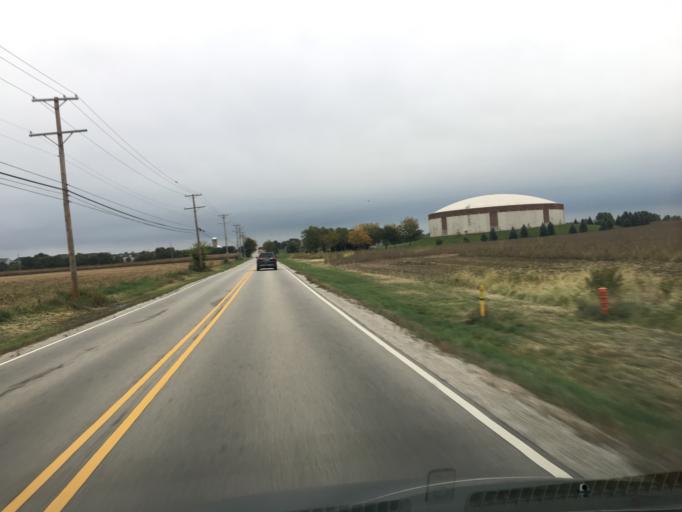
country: US
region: Illinois
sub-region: Will County
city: Plainfield
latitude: 41.6518
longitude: -88.1876
